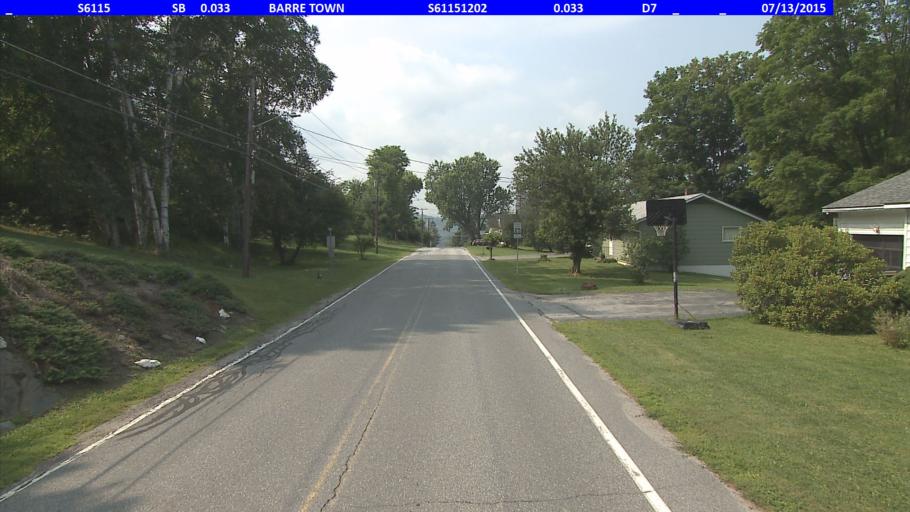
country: US
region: Vermont
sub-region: Washington County
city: Barre
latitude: 44.2012
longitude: -72.4875
